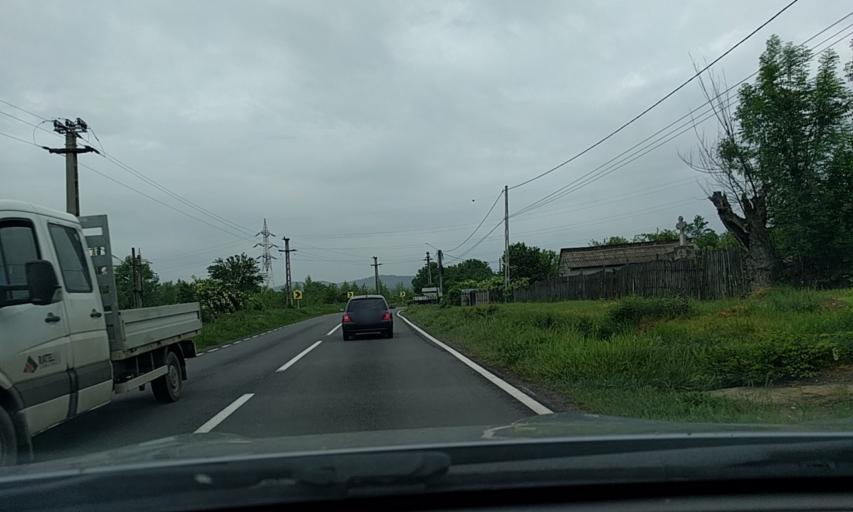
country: RO
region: Dambovita
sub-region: Comuna Vulcana-Pandele
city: Vulcana-Pandele
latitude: 45.0072
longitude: 25.4014
